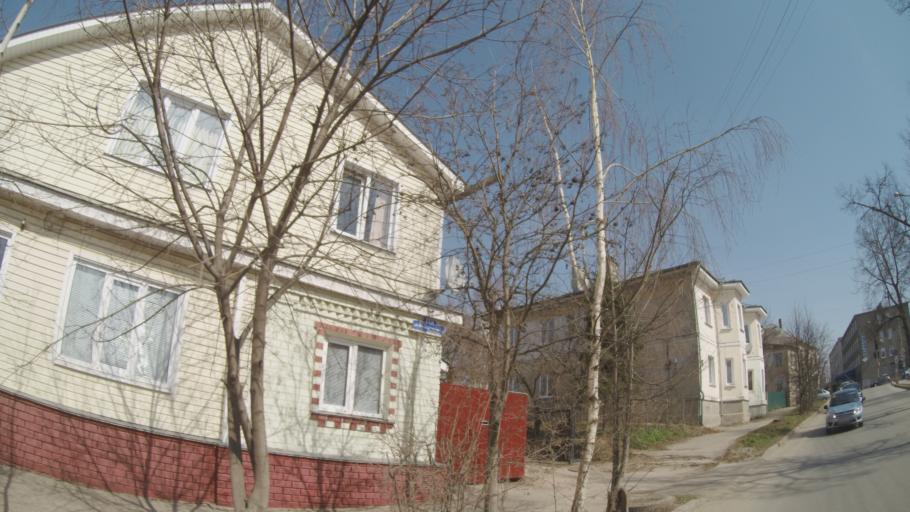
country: RU
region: Nizjnij Novgorod
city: Arzamas
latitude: 55.3873
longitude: 43.8185
